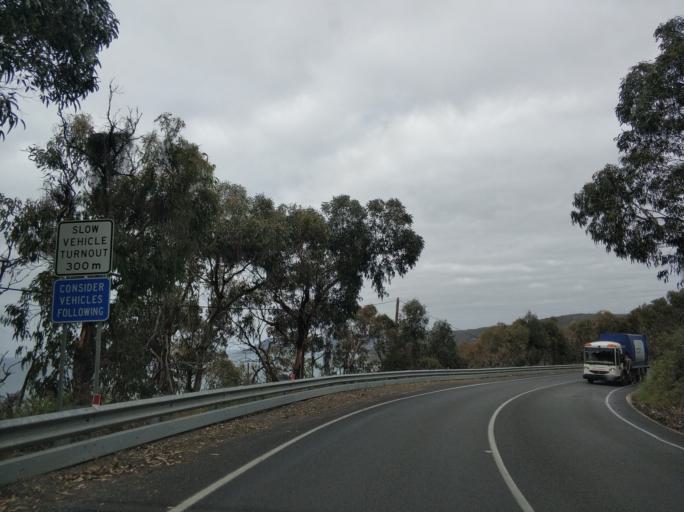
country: AU
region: Victoria
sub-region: Surf Coast
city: Anglesea
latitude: -38.4896
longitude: 144.0223
